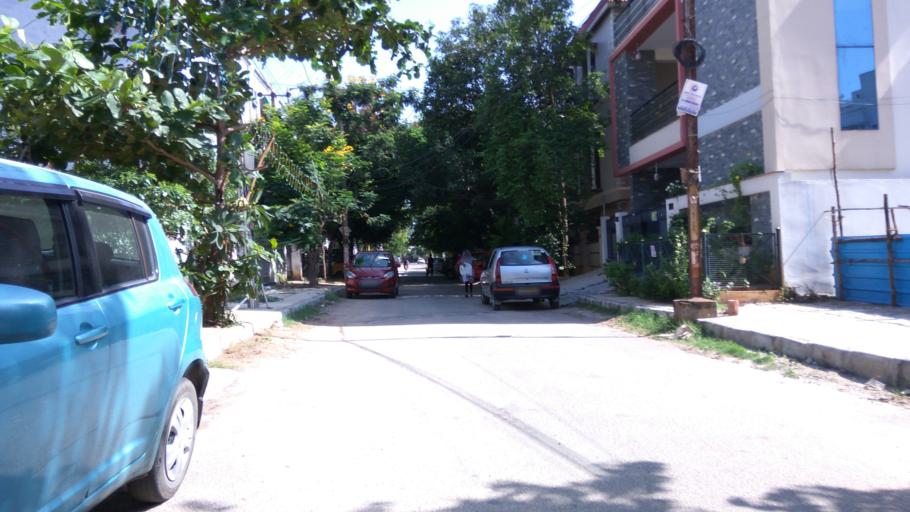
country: IN
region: Telangana
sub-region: Rangareddi
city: Kukatpalli
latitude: 17.4546
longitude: 78.4369
